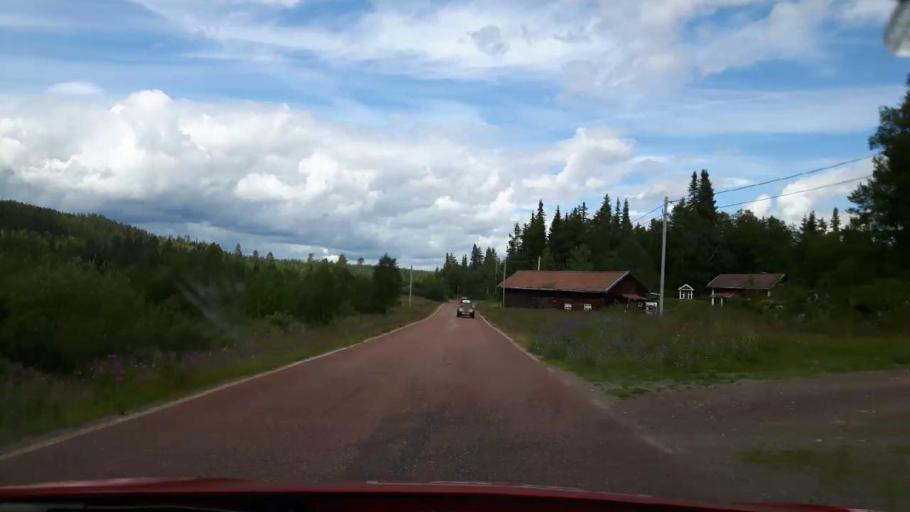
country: NO
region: Hedmark
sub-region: Trysil
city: Innbygda
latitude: 61.9968
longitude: 12.9815
